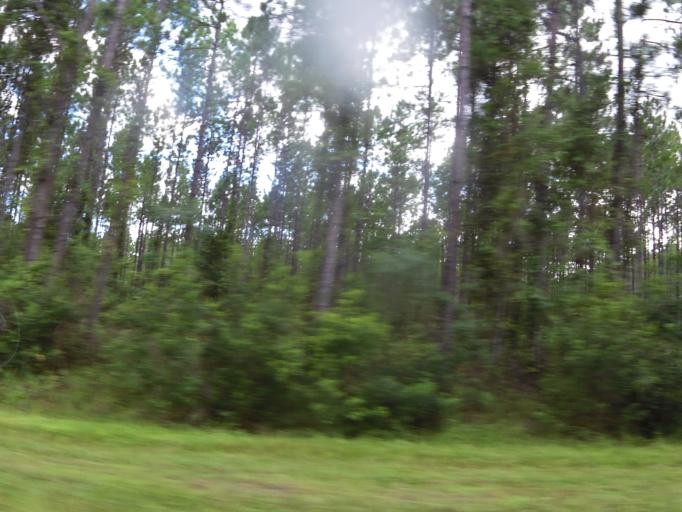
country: US
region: Florida
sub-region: Clay County
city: Green Cove Springs
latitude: 29.9957
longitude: -81.7340
